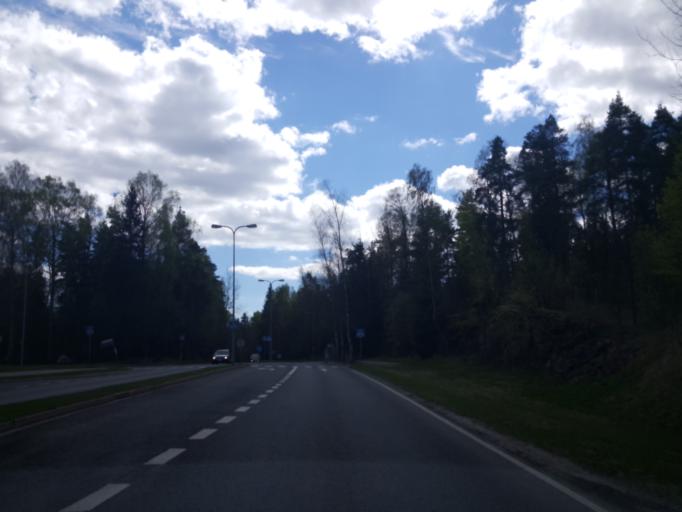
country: FI
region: Uusimaa
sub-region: Helsinki
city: Kilo
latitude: 60.2774
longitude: 24.8359
